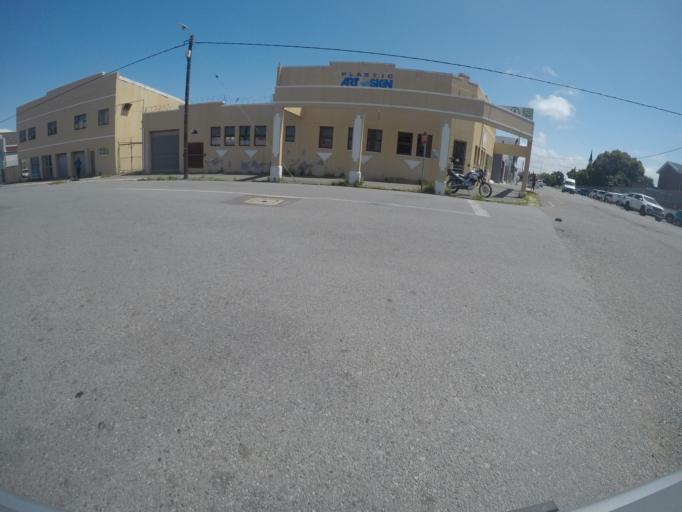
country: ZA
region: Eastern Cape
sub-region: Buffalo City Metropolitan Municipality
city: East London
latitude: -33.0069
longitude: 27.9032
